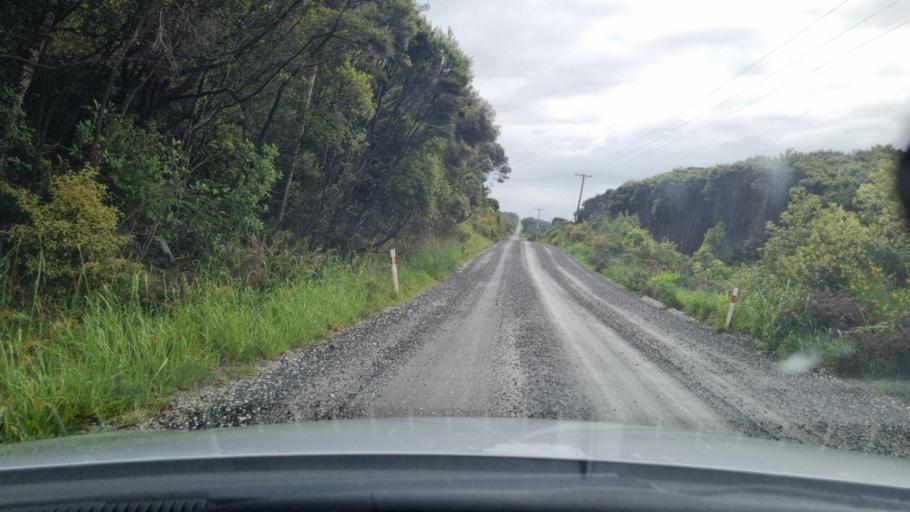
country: NZ
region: Southland
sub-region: Invercargill City
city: Bluff
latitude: -46.5409
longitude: 168.2638
